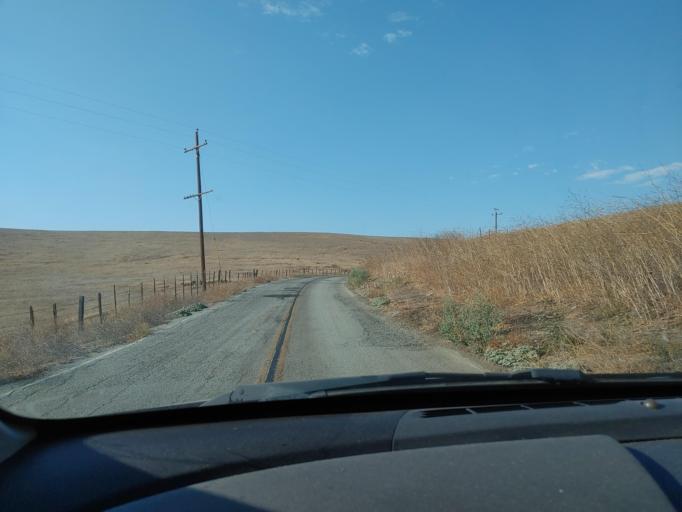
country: US
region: California
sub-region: San Benito County
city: Ridgemark
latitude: 36.8021
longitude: -121.3033
